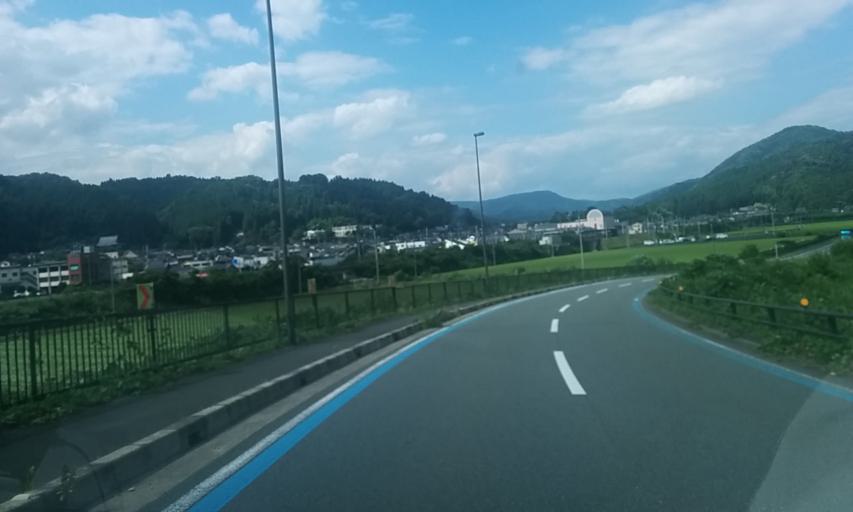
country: JP
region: Kyoto
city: Fukuchiyama
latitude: 35.3848
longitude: 135.1473
